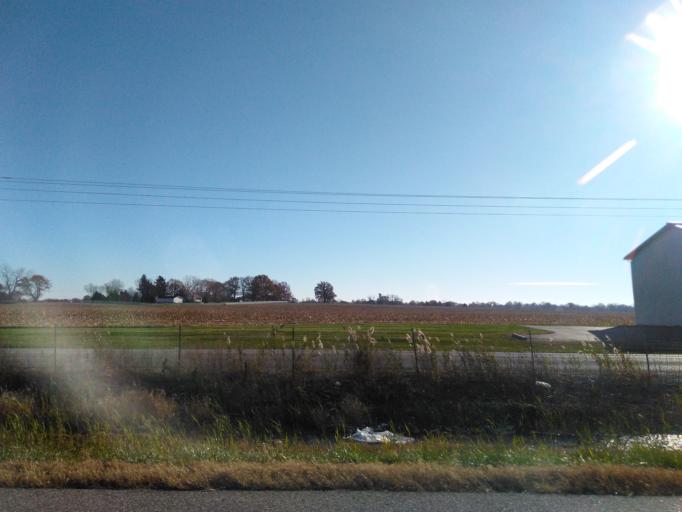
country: US
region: Illinois
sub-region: Madison County
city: Troy
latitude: 38.7425
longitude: -89.9096
